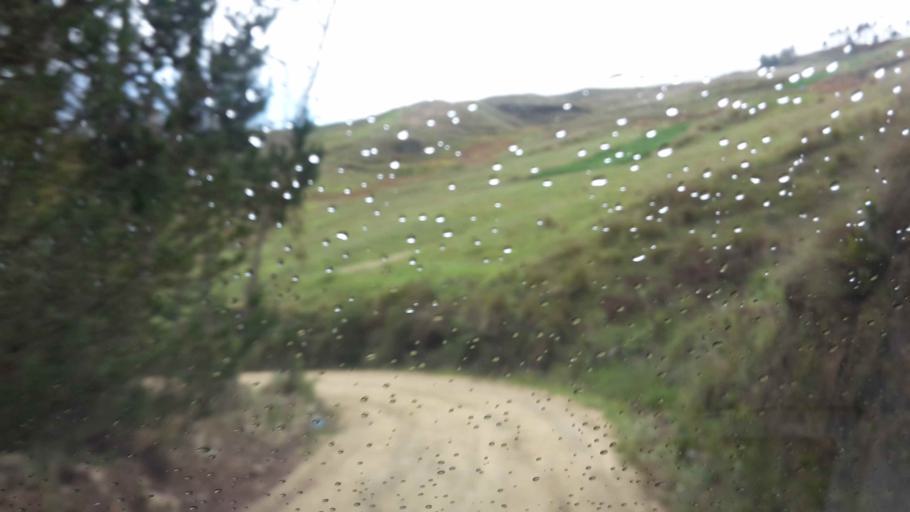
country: BO
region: Cochabamba
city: Cochabamba
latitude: -17.1359
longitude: -66.1052
